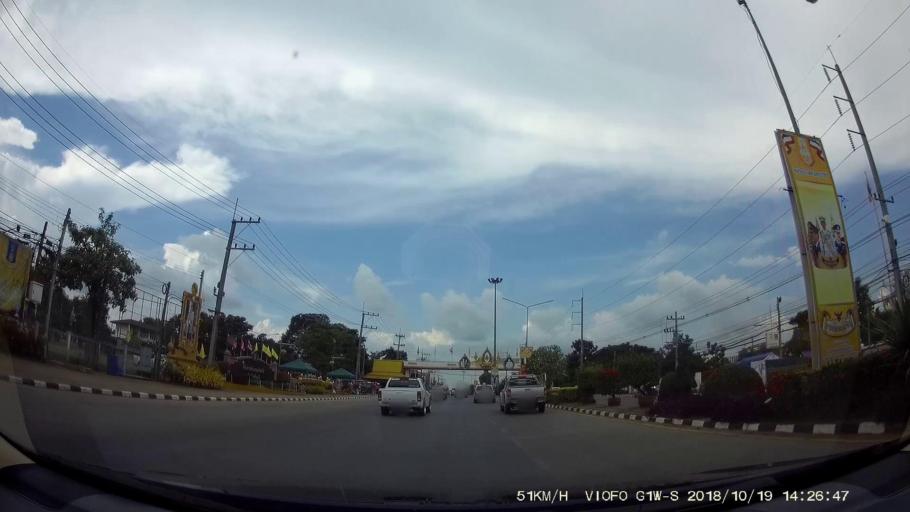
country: TH
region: Chaiyaphum
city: Kaeng Khro
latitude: 16.1087
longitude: 102.2589
